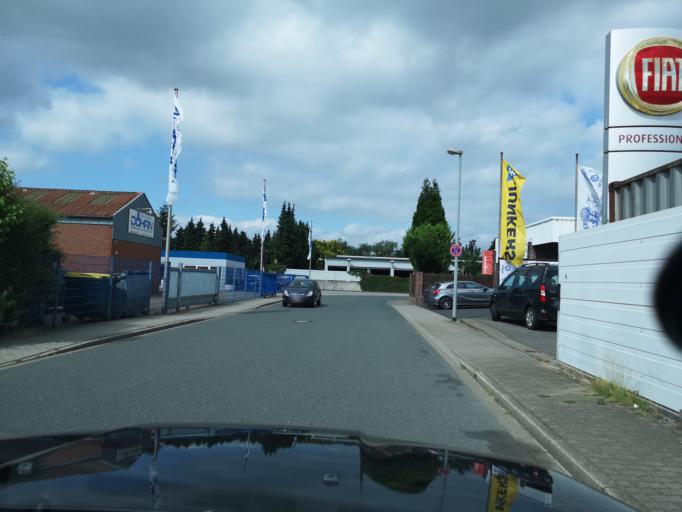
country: DE
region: North Rhine-Westphalia
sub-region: Regierungsbezirk Dusseldorf
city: Wesel
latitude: 51.6624
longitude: 6.6458
